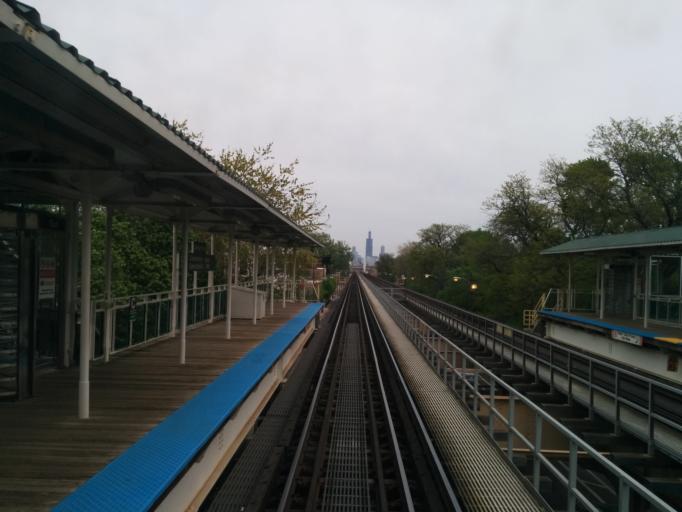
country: US
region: Illinois
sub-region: Cook County
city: Cicero
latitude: 41.8849
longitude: -87.7155
